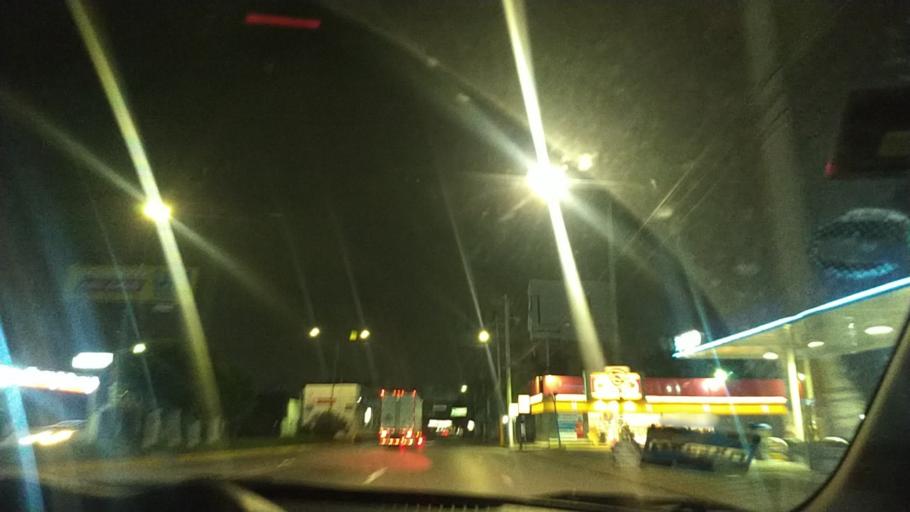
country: MX
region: Mexico
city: Ecatepec
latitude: 19.6243
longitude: -99.0761
